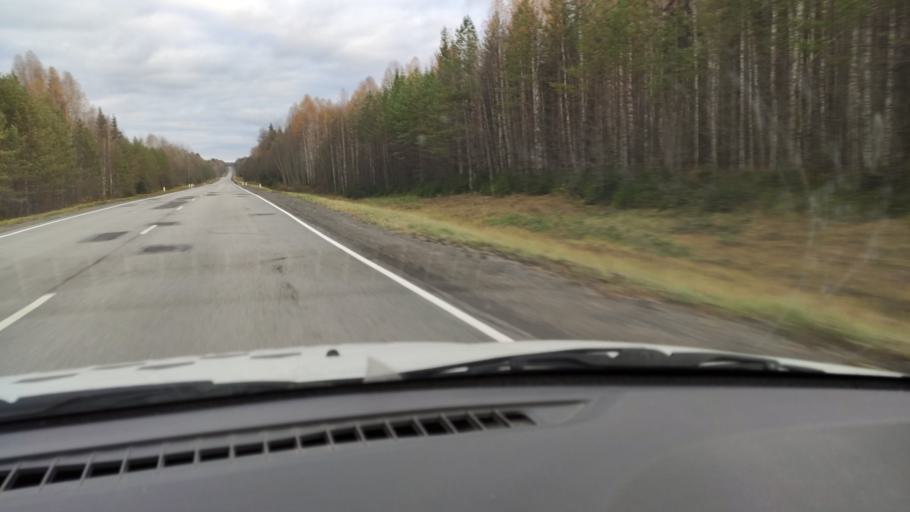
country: RU
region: Kirov
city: Dubrovka
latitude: 58.9040
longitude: 51.2759
